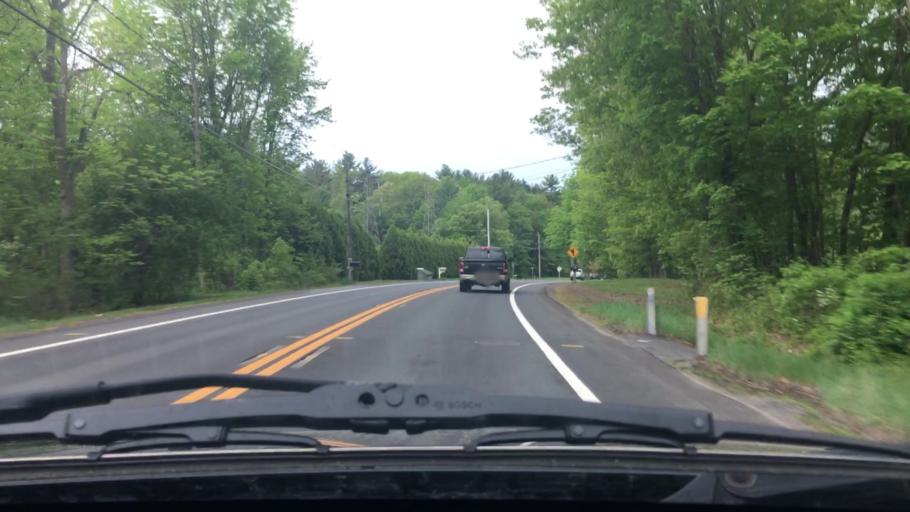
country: US
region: Massachusetts
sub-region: Franklin County
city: Leverett
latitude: 42.4621
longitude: -72.5176
